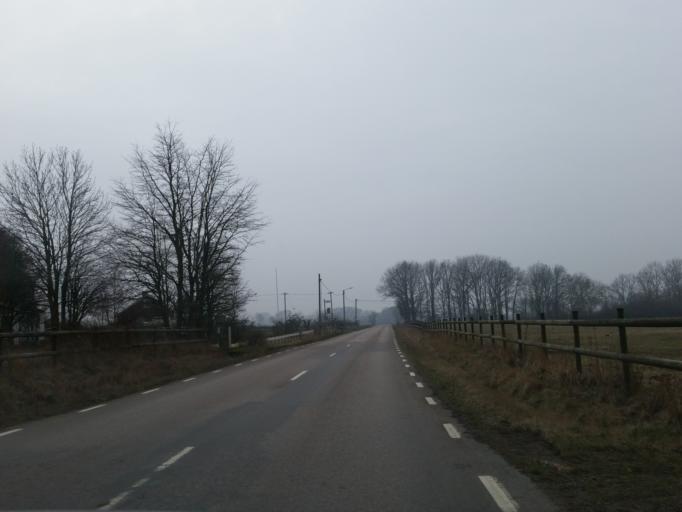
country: SE
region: Kalmar
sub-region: Morbylanga Kommun
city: Moerbylanga
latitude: 56.4271
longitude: 16.4177
